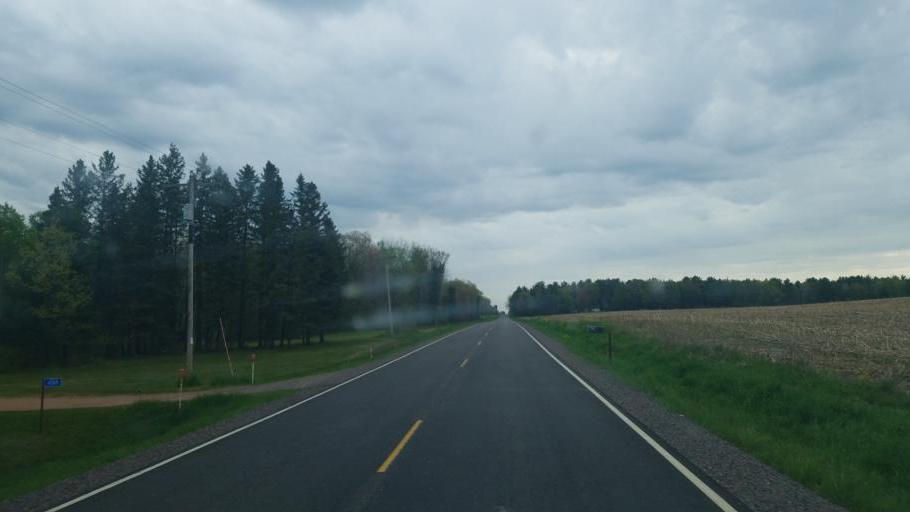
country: US
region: Wisconsin
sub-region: Wood County
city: Marshfield
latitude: 44.4738
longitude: -90.2801
